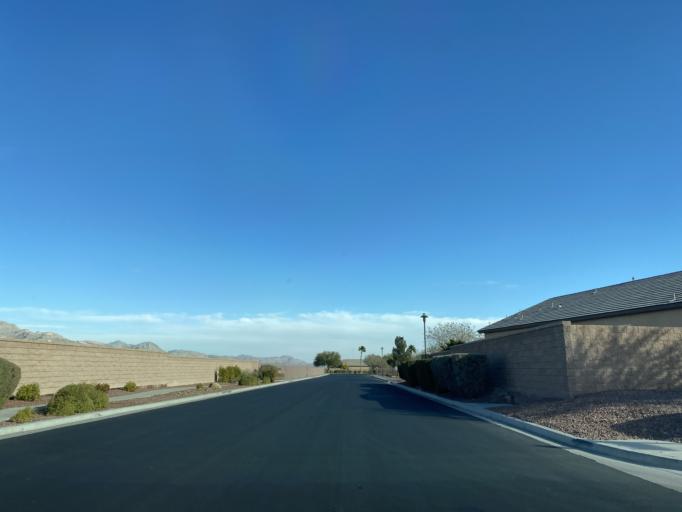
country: US
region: Nevada
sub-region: Clark County
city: North Las Vegas
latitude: 36.3211
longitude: -115.2461
